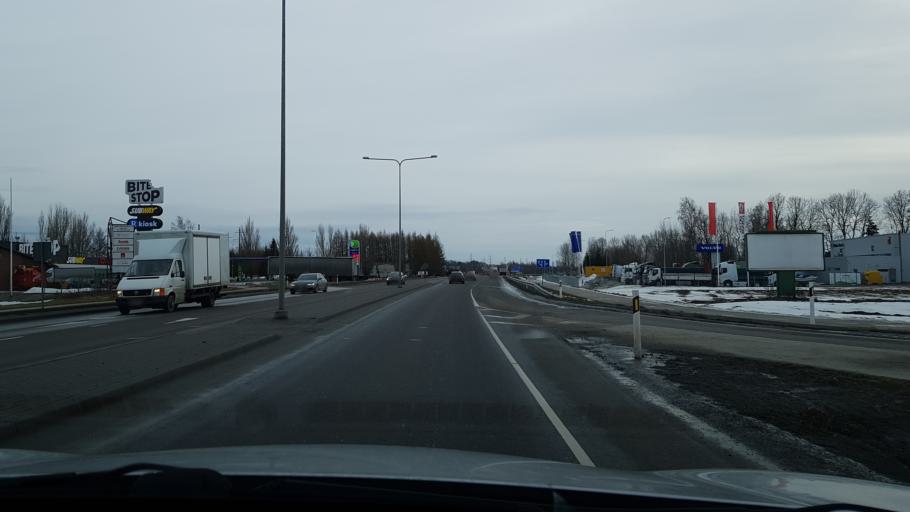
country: EE
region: Tartu
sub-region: Tartu linn
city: Tartu
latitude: 58.3766
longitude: 26.6771
